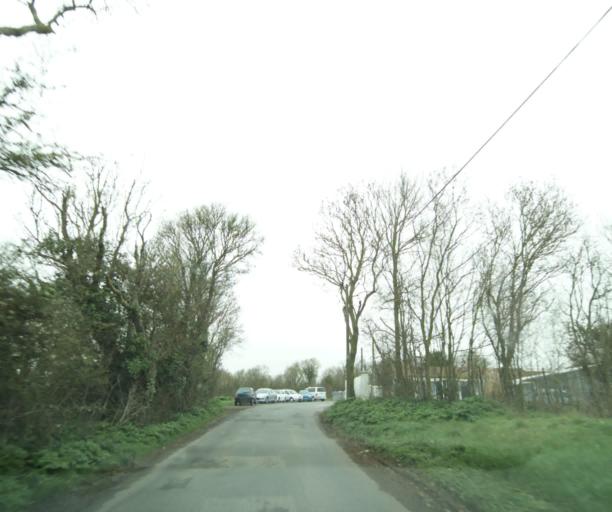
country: FR
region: Poitou-Charentes
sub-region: Departement de la Charente-Maritime
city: Lagord
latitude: 46.1831
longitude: -1.1378
